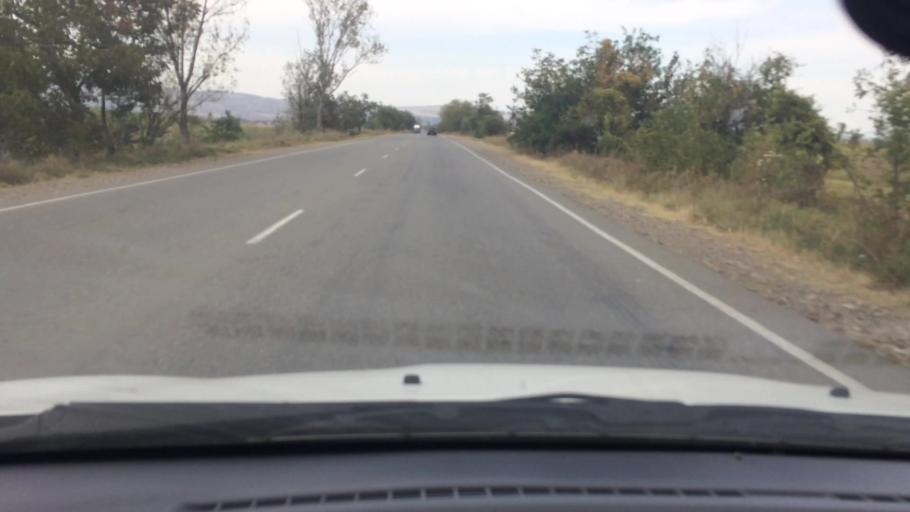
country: GE
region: Kvemo Kartli
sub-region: Marneuli
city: Marneuli
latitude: 41.5571
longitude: 44.7760
